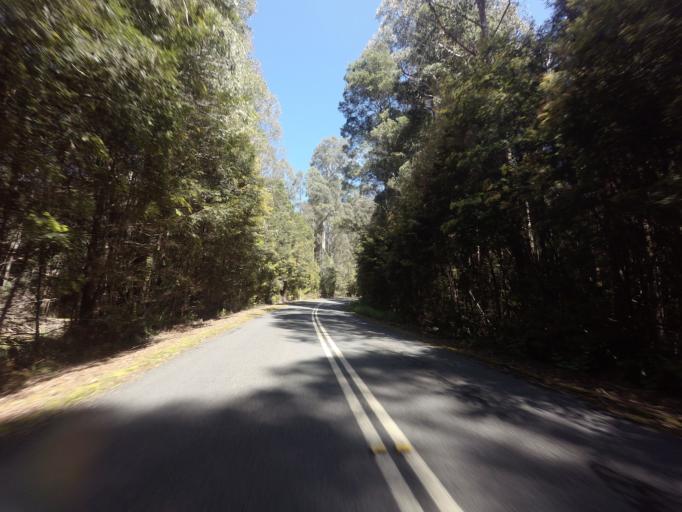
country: AU
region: Tasmania
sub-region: Huon Valley
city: Geeveston
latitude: -42.8202
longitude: 146.3026
